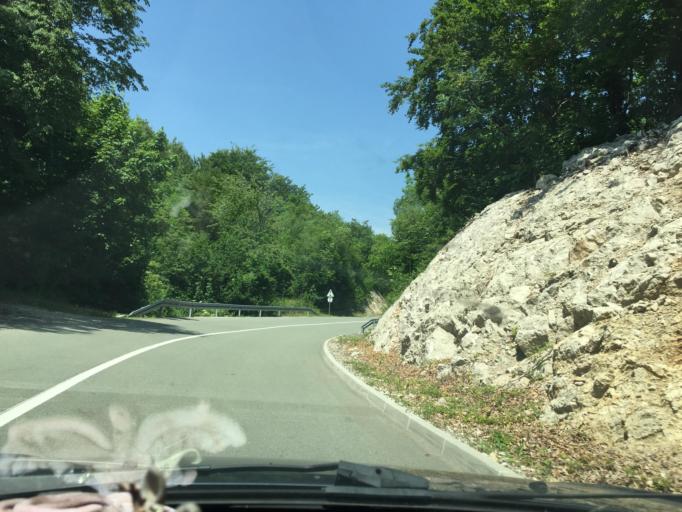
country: HR
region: Primorsko-Goranska
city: Matulji
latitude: 45.4091
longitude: 14.2527
